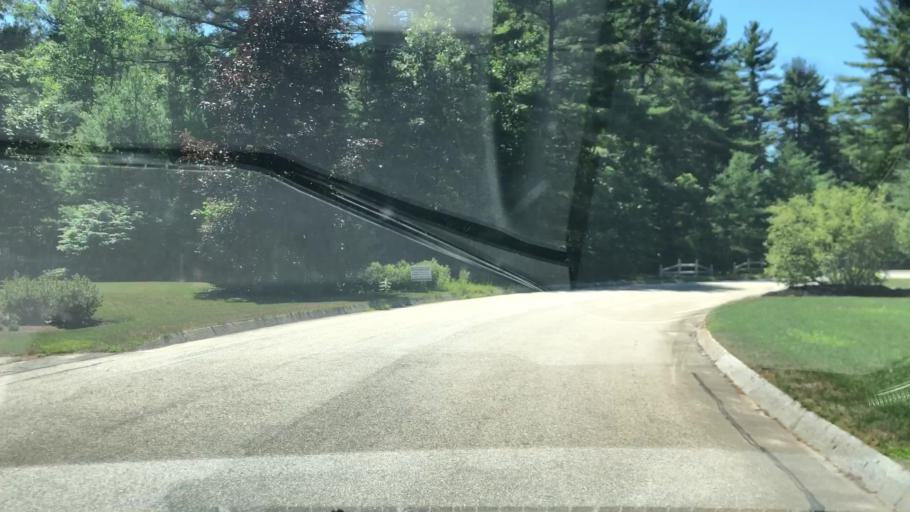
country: US
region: New Hampshire
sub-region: Hillsborough County
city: Milford
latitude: 42.8423
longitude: -71.5753
